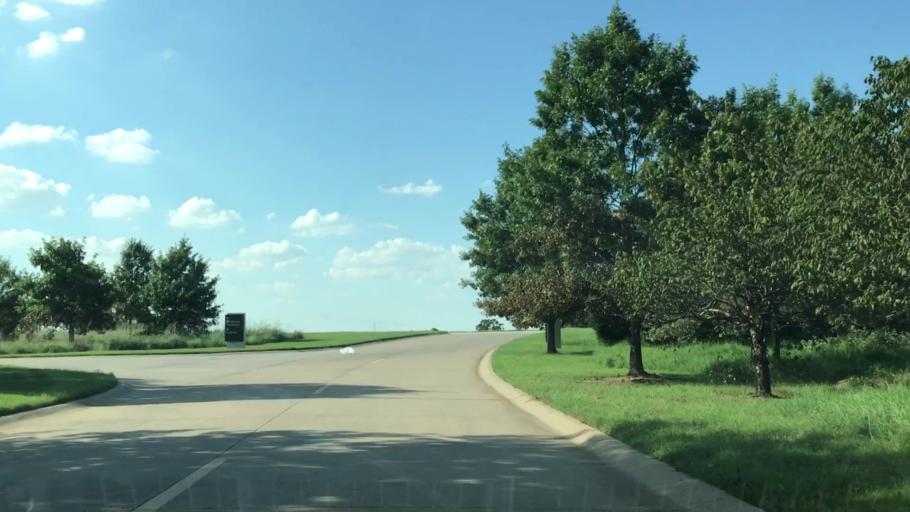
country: US
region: Texas
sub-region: Denton County
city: Trophy Club
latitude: 32.9858
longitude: -97.1860
